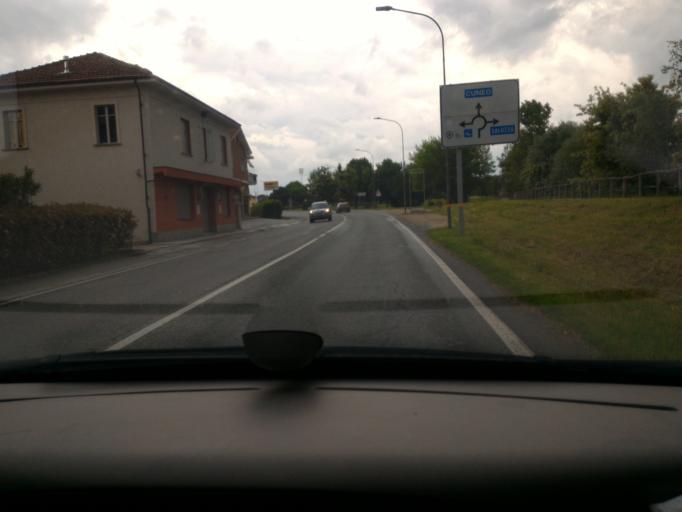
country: IT
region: Piedmont
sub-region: Provincia di Cuneo
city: Savigliano
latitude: 44.6429
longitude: 7.6499
